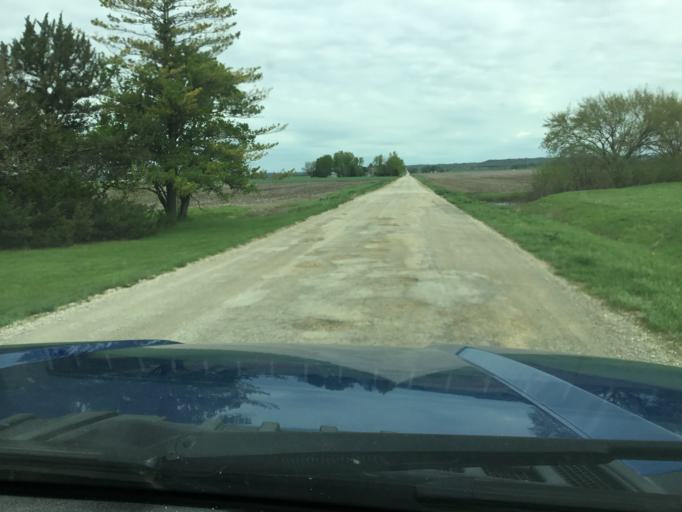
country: US
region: Kansas
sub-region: Douglas County
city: Lawrence
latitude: 39.0052
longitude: -95.2241
